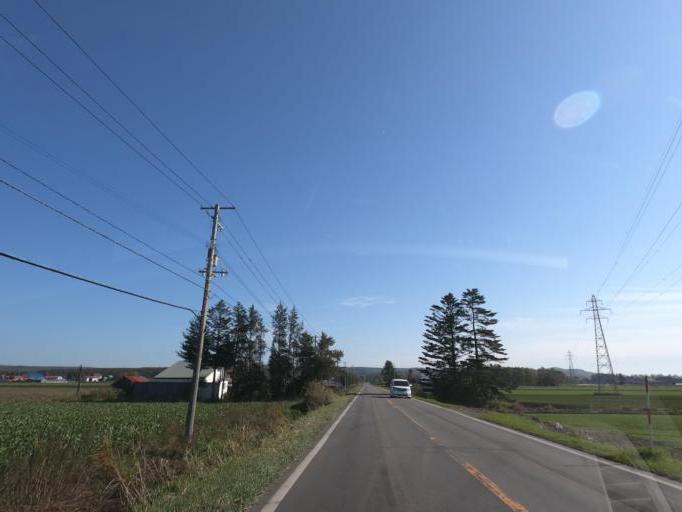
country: JP
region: Hokkaido
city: Otofuke
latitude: 42.9595
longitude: 143.2361
